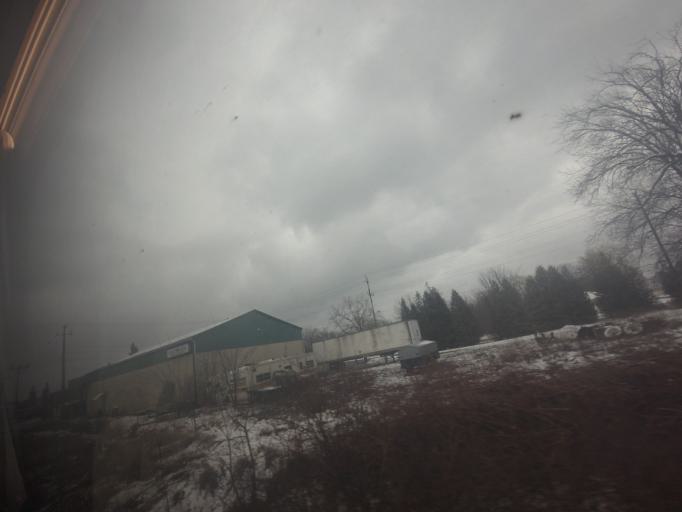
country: CA
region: Ontario
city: Cobourg
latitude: 43.9484
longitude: -78.2862
